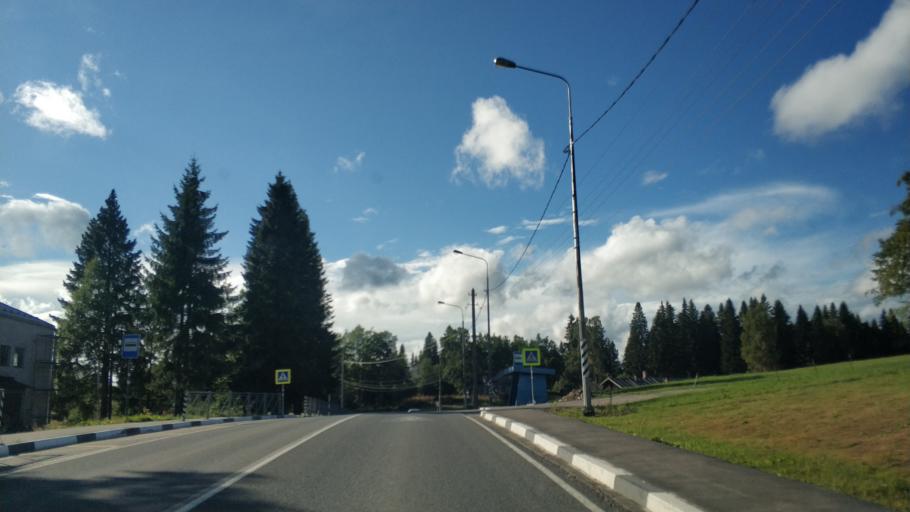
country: RU
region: Republic of Karelia
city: Lakhdenpokh'ya
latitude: 61.5226
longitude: 30.1848
